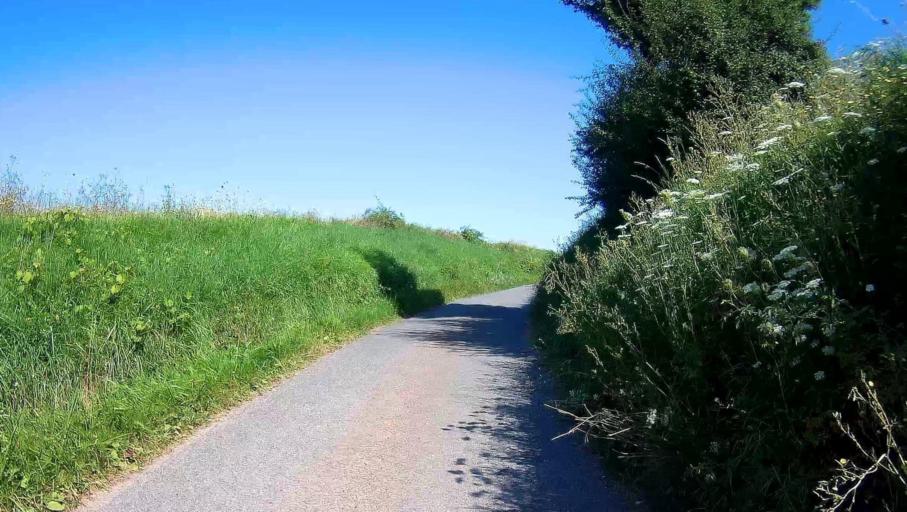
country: FR
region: Bourgogne
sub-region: Departement de Saone-et-Loire
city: Couches
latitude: 46.8480
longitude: 4.5688
